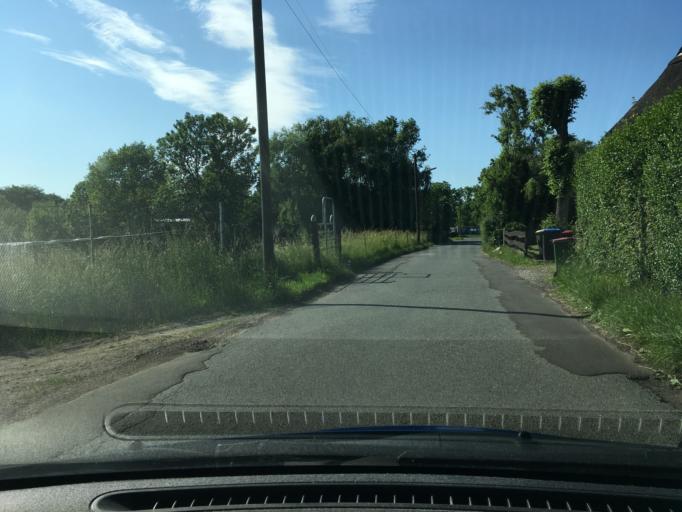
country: DE
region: Hamburg
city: Harburg
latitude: 53.4770
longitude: 10.0087
